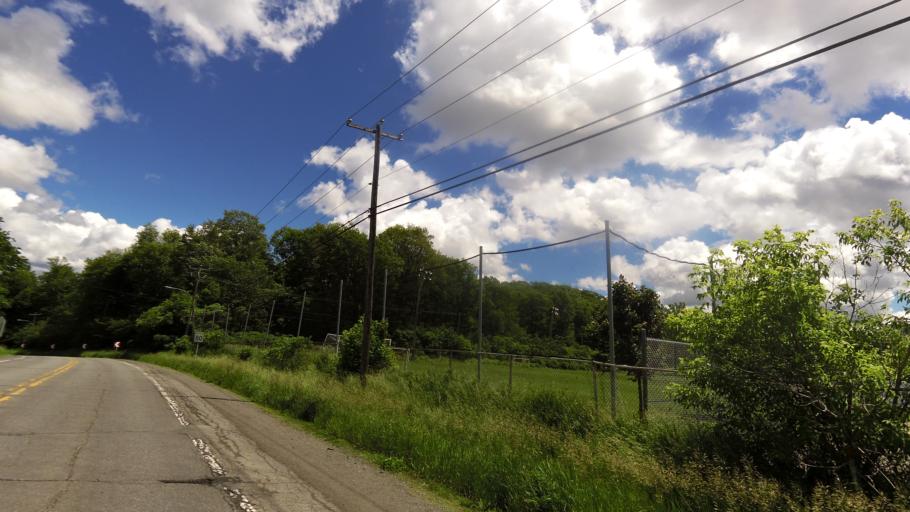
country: CA
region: Quebec
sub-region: Laurentides
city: Oka
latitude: 45.4901
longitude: -74.0347
